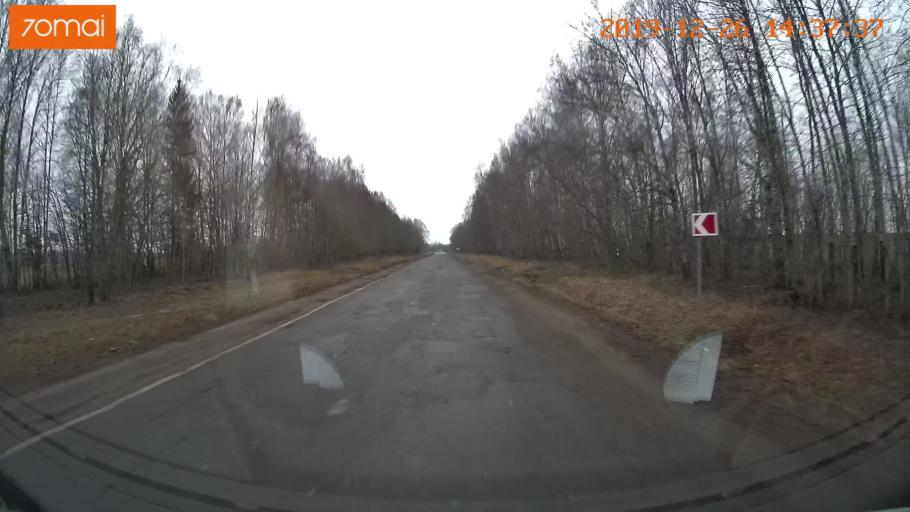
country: RU
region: Jaroslavl
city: Poshekhon'ye
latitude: 58.4009
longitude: 38.9718
